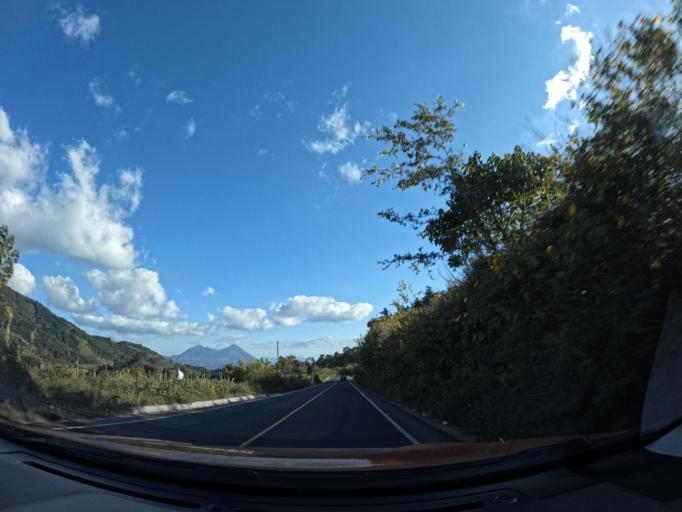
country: GT
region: Sacatepequez
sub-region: Municipio de Santa Maria de Jesus
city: Santa Maria de Jesus
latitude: 14.4836
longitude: -90.7029
